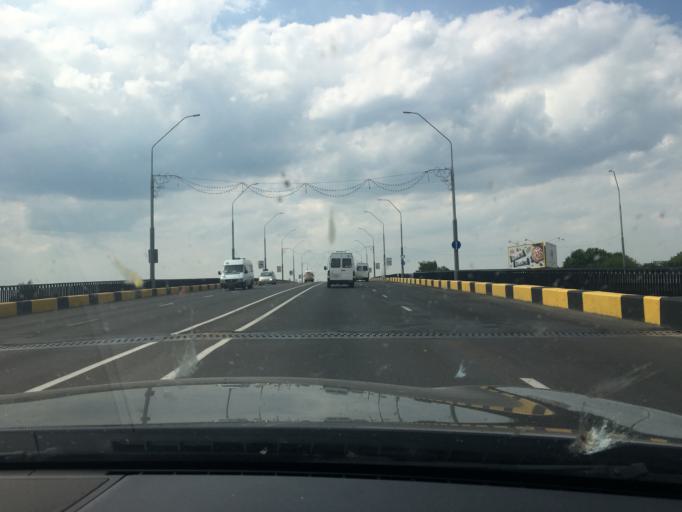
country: BY
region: Brest
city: Brest
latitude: 52.0971
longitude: 23.6806
